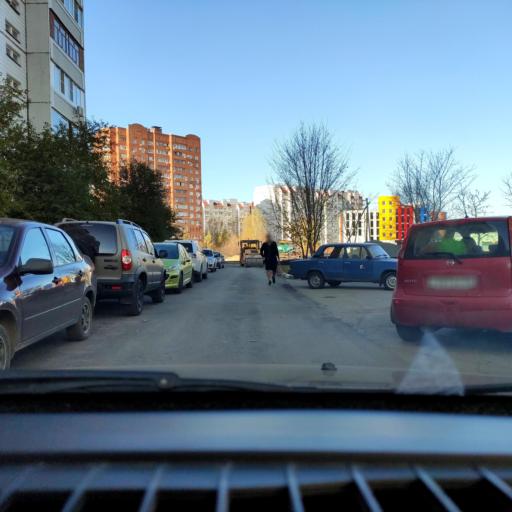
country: RU
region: Samara
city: Tol'yatti
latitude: 53.5467
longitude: 49.3286
